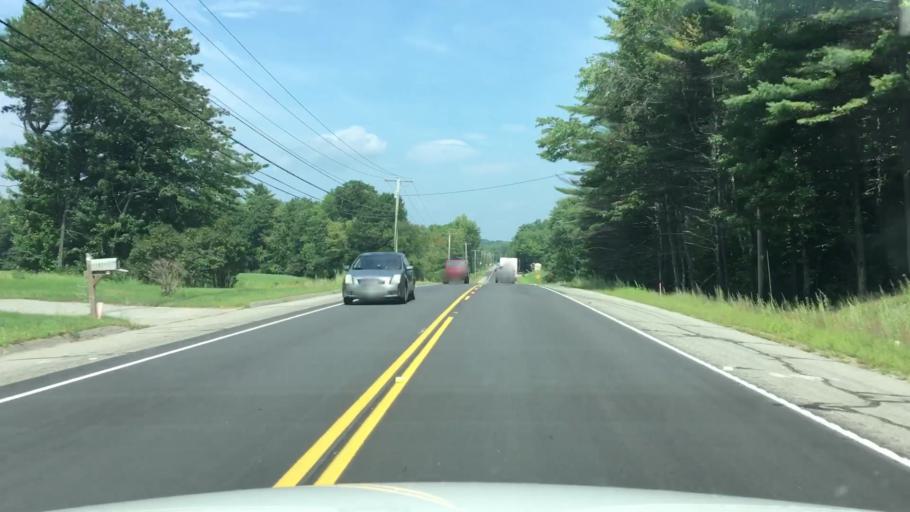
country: US
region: Maine
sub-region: Androscoggin County
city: Turner
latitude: 44.2069
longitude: -70.2458
